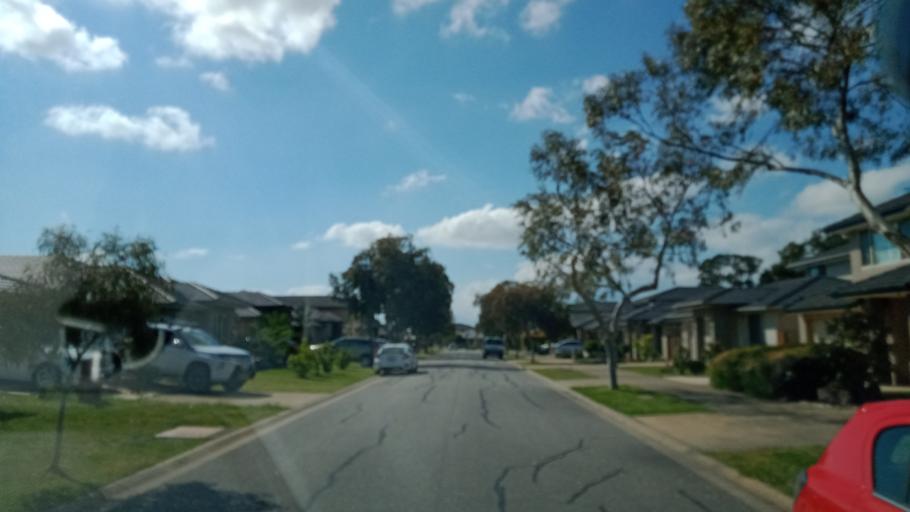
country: AU
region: Victoria
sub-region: Frankston
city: Sandhurst
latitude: -38.0863
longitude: 145.2120
